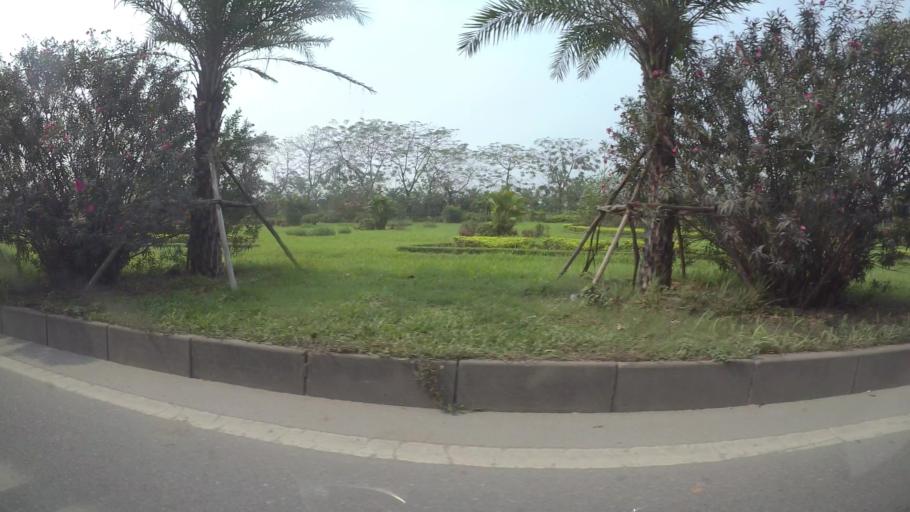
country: VN
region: Ha Noi
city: Thanh Xuan
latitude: 21.0043
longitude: 105.7768
